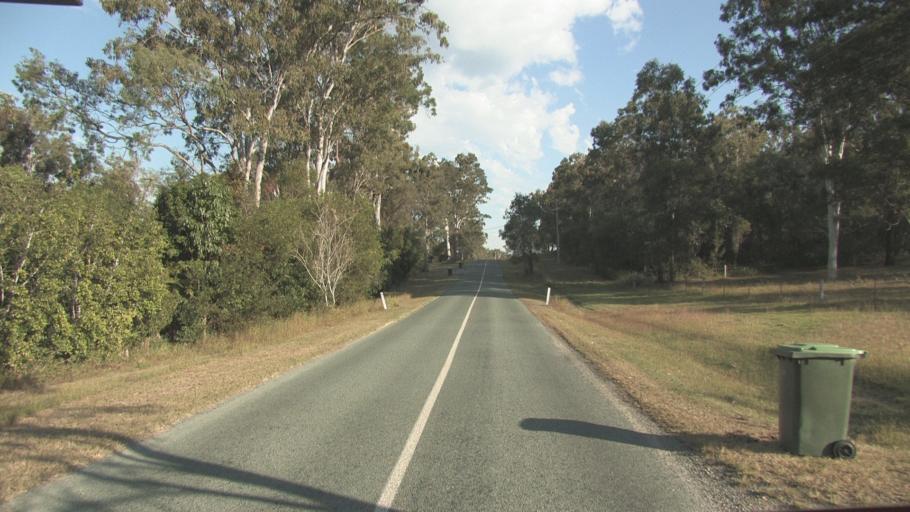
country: AU
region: Queensland
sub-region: Gold Coast
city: Ormeau Hills
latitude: -27.8329
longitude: 153.1698
